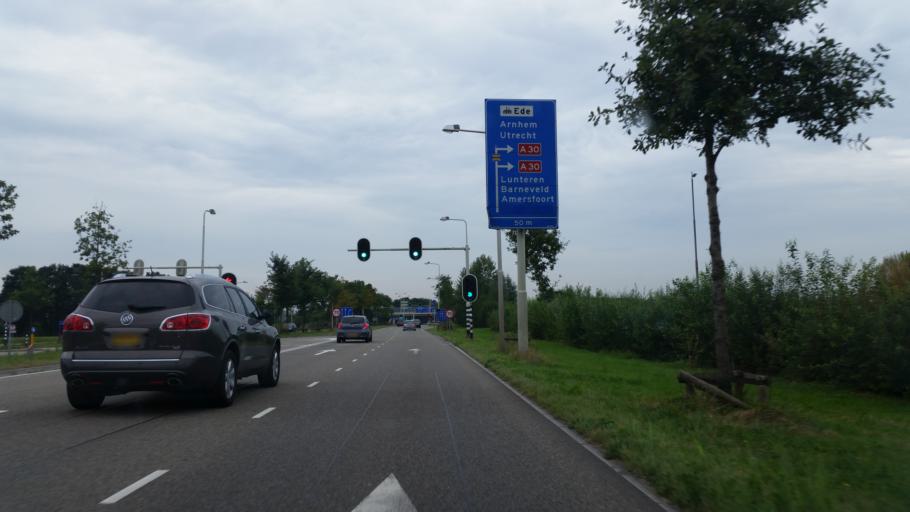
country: NL
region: Gelderland
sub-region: Gemeente Ede
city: Ede
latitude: 52.0464
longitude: 5.6249
